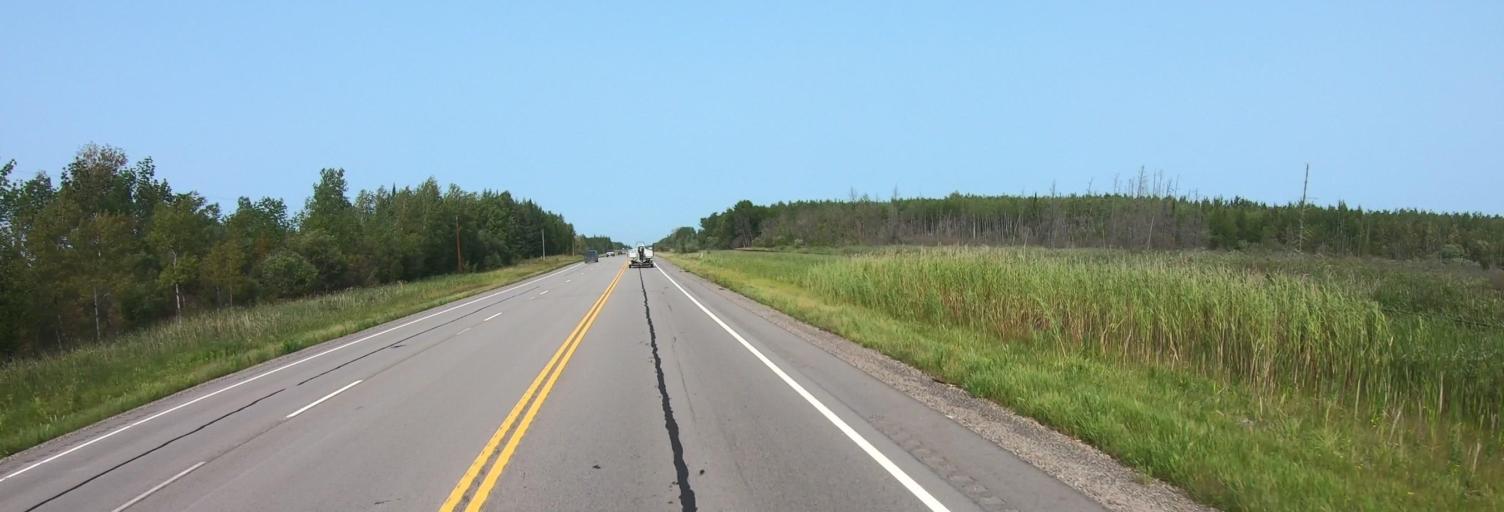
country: CA
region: Ontario
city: Fort Frances
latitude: 48.4400
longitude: -93.2546
